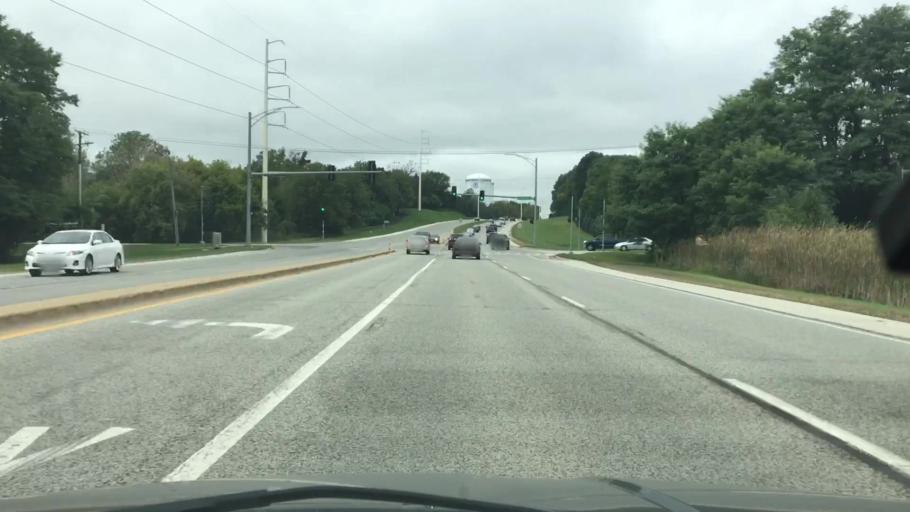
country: US
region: Illinois
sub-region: DuPage County
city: Woodridge
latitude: 41.7496
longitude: -88.0733
